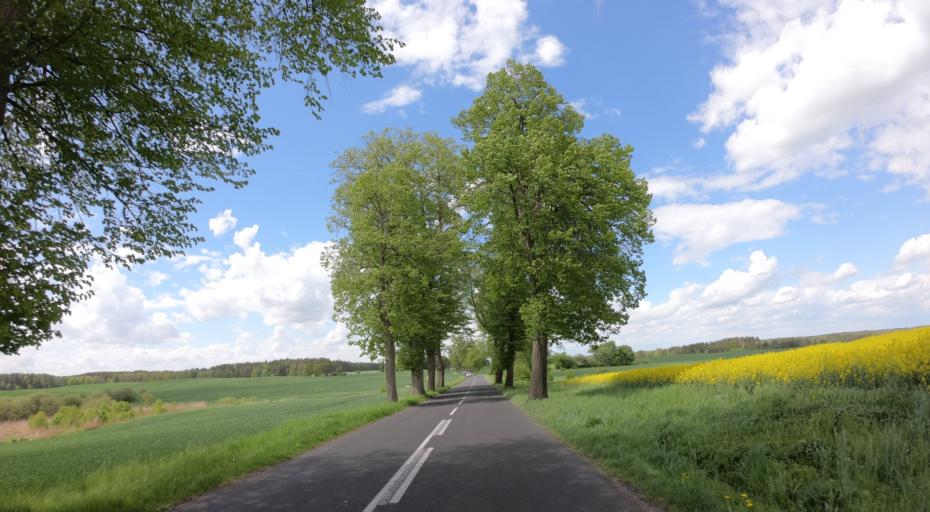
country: PL
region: West Pomeranian Voivodeship
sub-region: Powiat drawski
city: Drawsko Pomorskie
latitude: 53.5941
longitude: 15.7236
